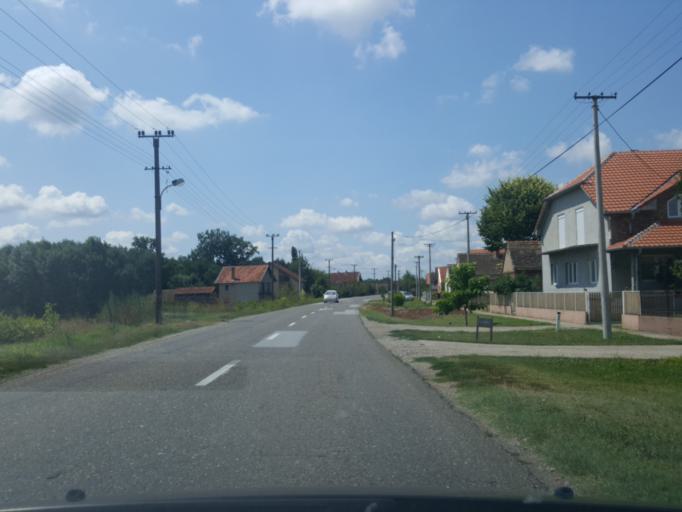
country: RS
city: Salas Nocajski
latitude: 44.9307
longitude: 19.5649
